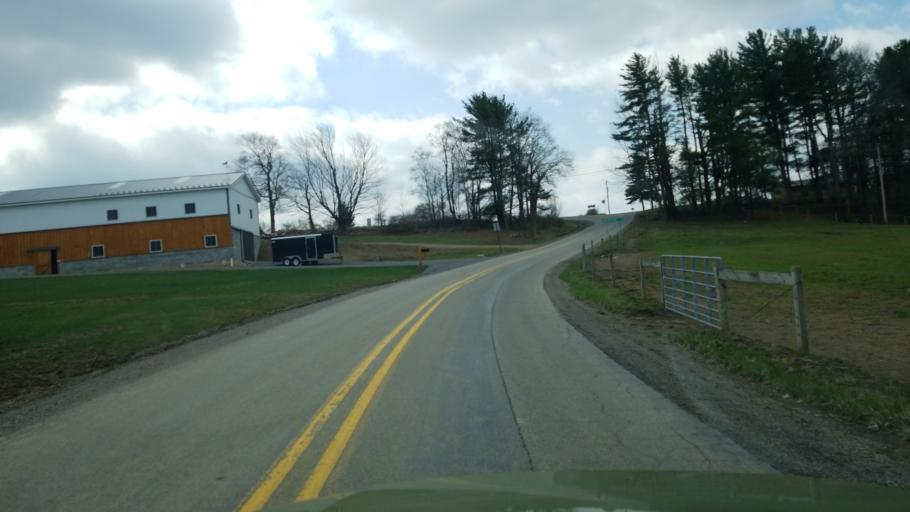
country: US
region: Pennsylvania
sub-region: Jefferson County
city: Brockway
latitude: 41.2763
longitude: -78.8424
